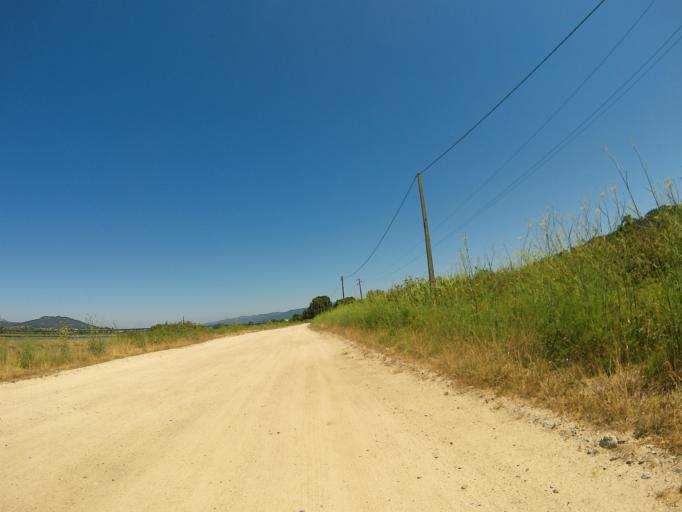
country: PT
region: Viana do Castelo
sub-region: Viana do Castelo
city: Meadela
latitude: 41.6880
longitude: -8.8007
